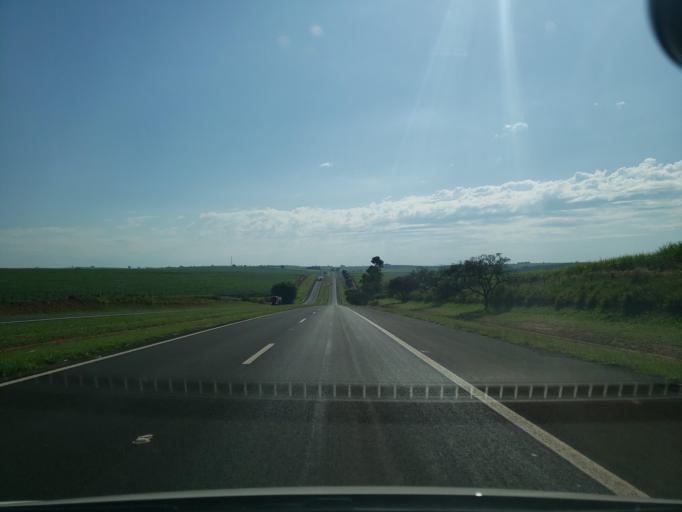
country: BR
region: Sao Paulo
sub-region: Promissao
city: Promissao
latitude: -21.5367
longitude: -49.9760
